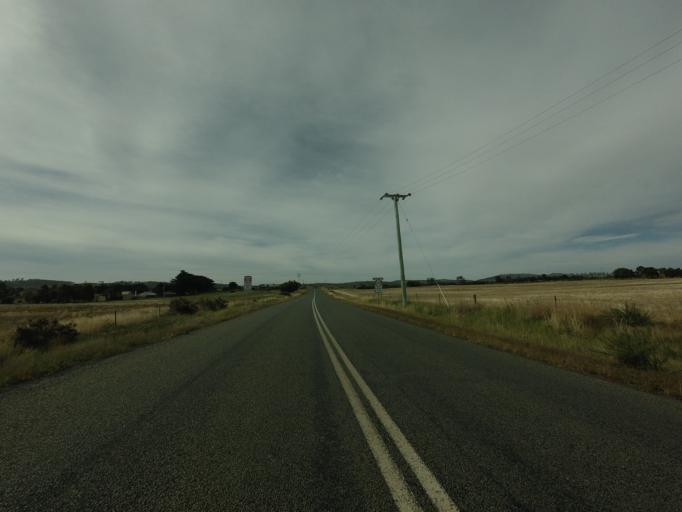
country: AU
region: Tasmania
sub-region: Brighton
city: Bridgewater
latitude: -42.3110
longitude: 147.3703
